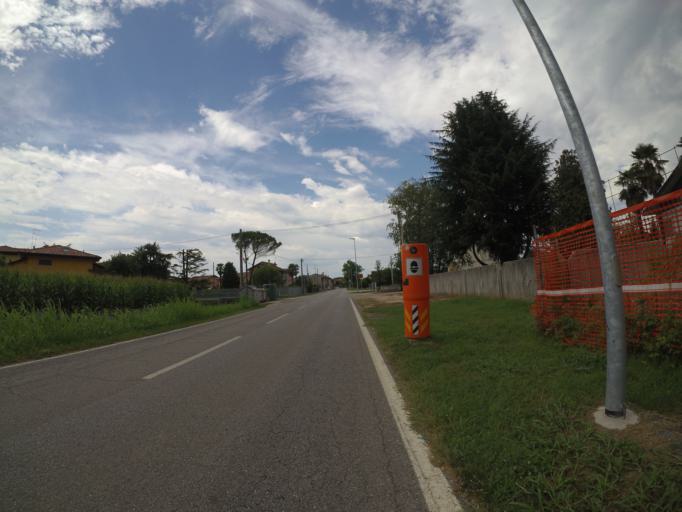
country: IT
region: Friuli Venezia Giulia
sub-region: Provincia di Udine
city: Talmassons
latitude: 45.9265
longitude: 13.1283
